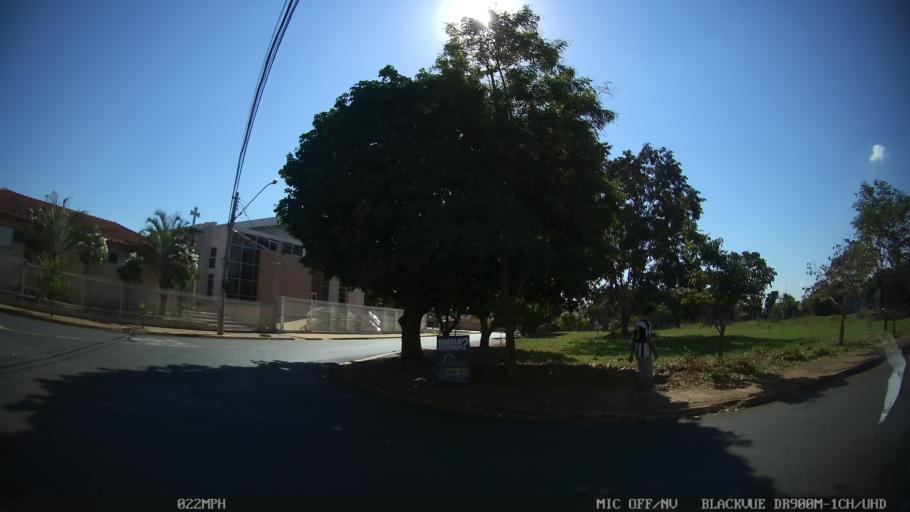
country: BR
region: Sao Paulo
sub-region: Ribeirao Preto
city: Ribeirao Preto
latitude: -21.2185
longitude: -47.7651
